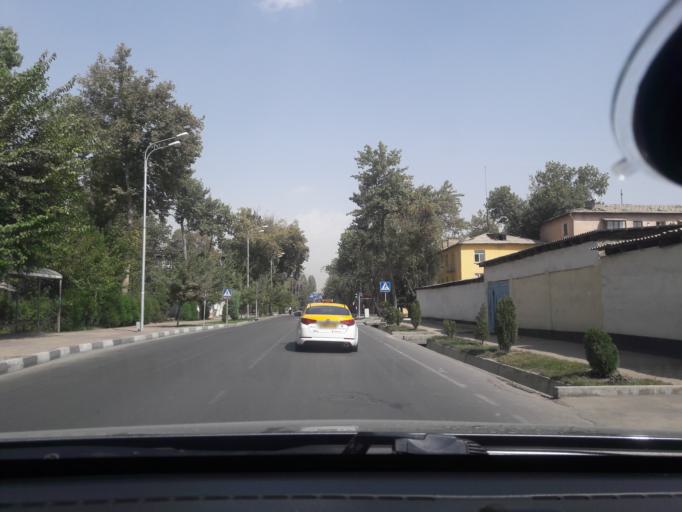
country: TJ
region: Dushanbe
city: Dushanbe
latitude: 38.5653
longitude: 68.7633
